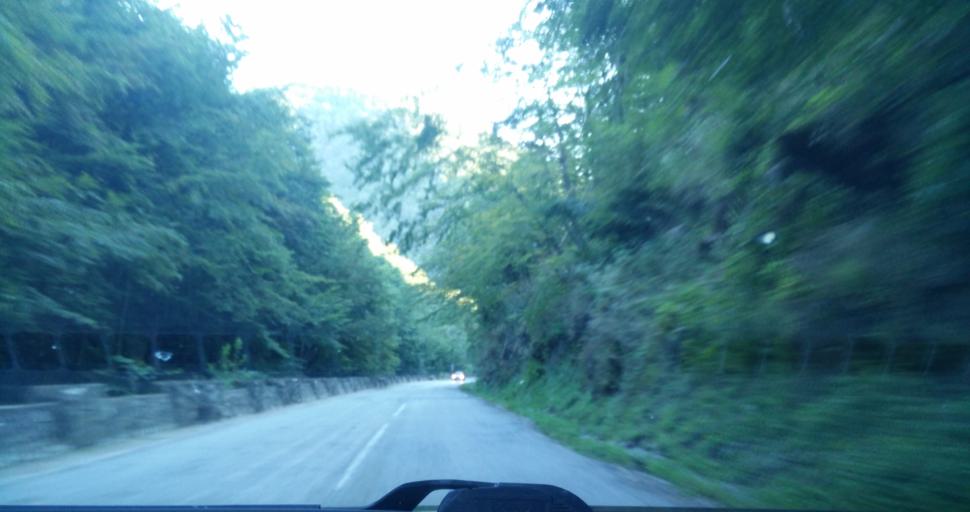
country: RO
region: Bihor
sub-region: Oras Nucet
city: Nucet
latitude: 46.4846
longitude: 22.5972
